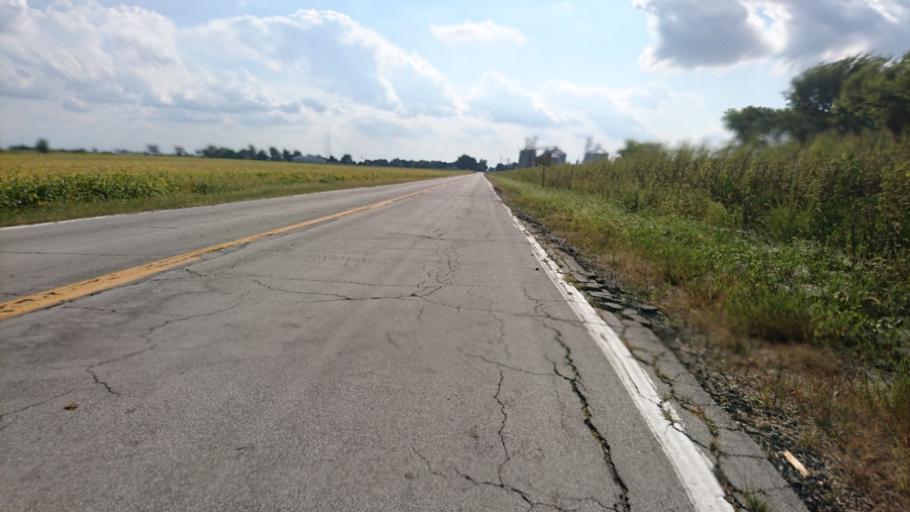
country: US
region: Illinois
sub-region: Logan County
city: Atlanta
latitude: 40.3243
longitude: -89.1581
